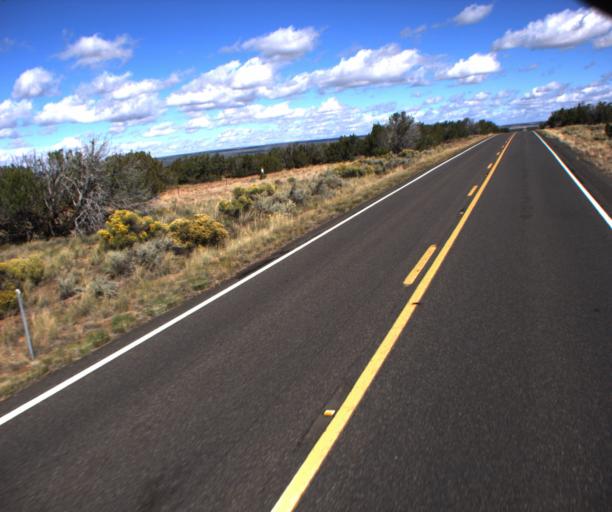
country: US
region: Arizona
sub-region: Apache County
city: Saint Johns
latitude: 34.8454
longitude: -109.2376
